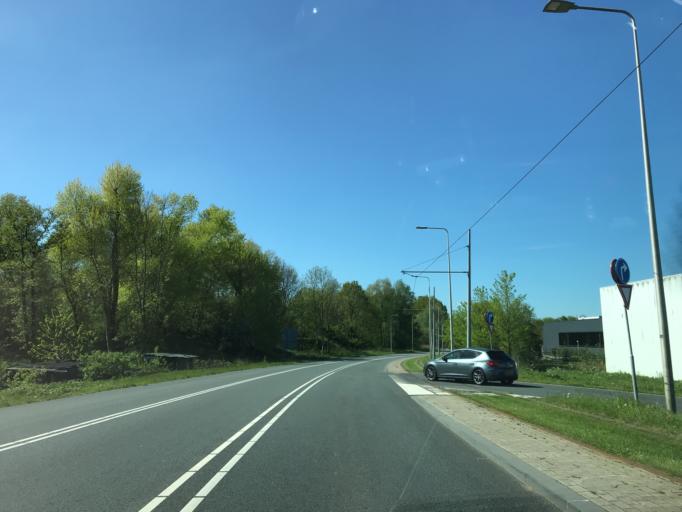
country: NL
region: North Holland
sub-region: Gemeente Diemen
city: Diemen
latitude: 52.3299
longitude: 4.9749
